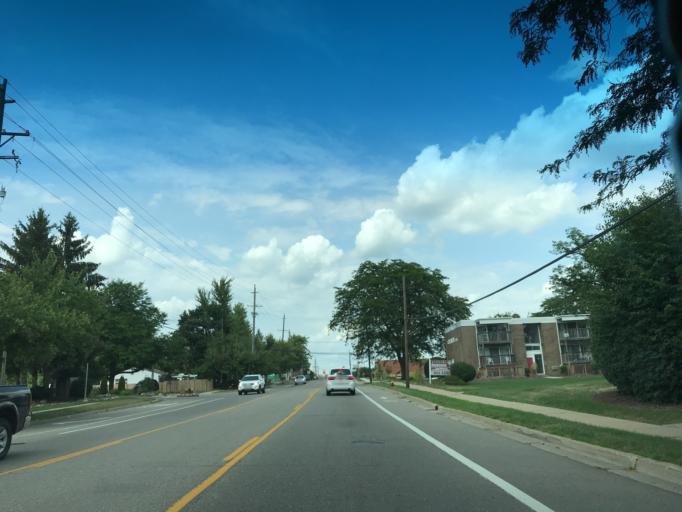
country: US
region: Michigan
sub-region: Washtenaw County
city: Ypsilanti
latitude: 42.2479
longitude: -83.6610
